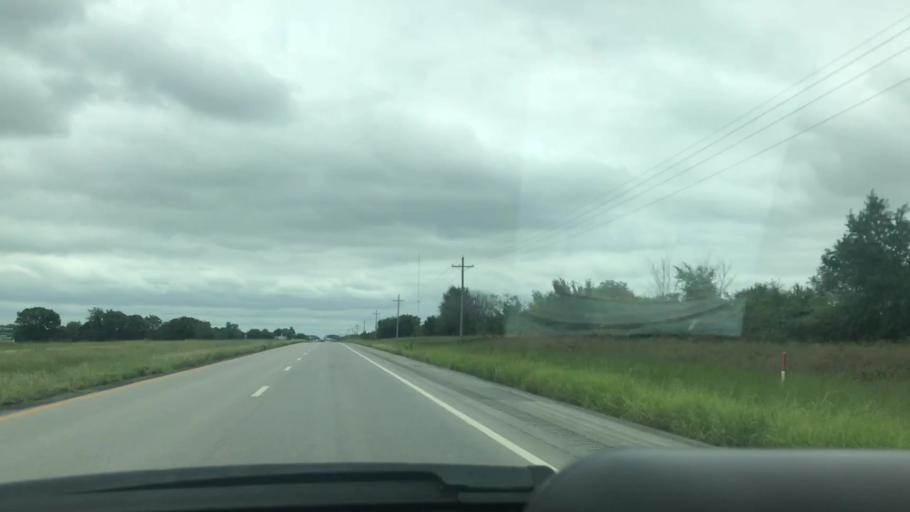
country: US
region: Oklahoma
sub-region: Mayes County
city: Pryor
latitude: 36.4134
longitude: -95.2802
